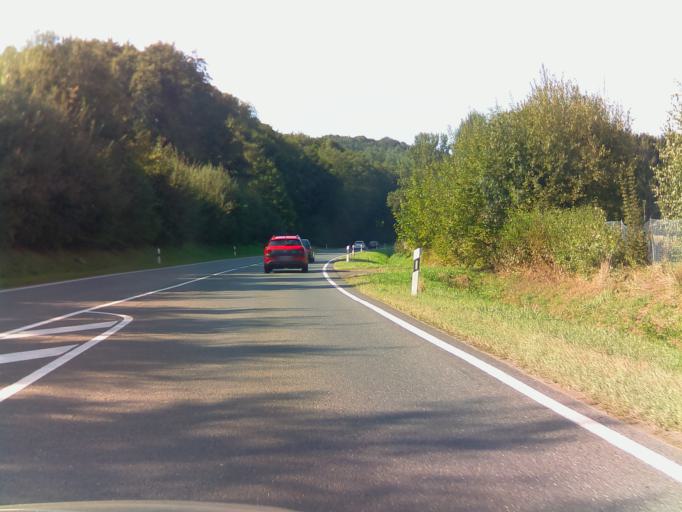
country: DE
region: Bavaria
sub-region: Upper Franconia
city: Michelau
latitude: 50.1490
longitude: 11.1319
